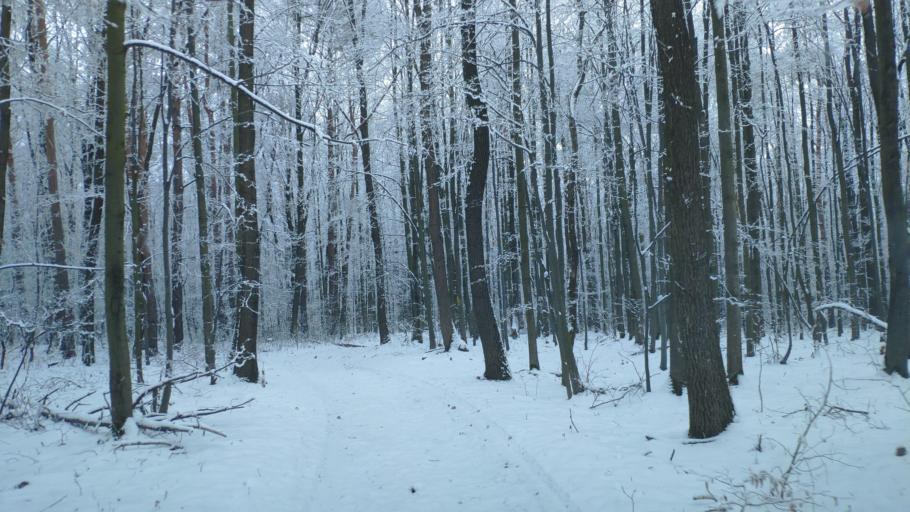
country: SK
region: Kosicky
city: Kosice
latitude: 48.6604
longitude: 21.1853
